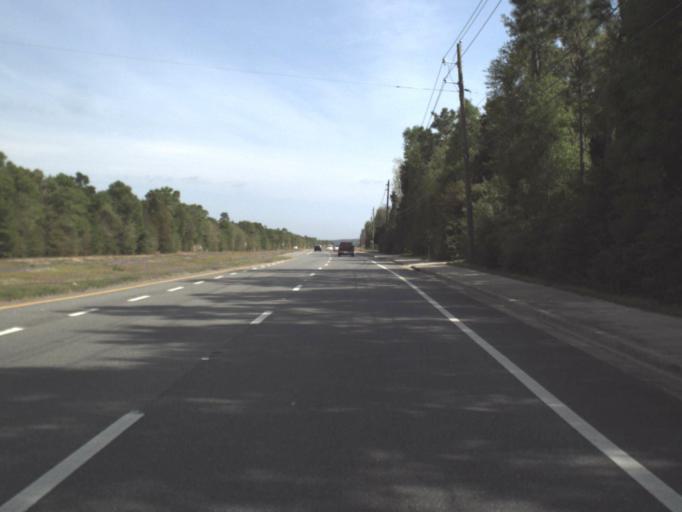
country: US
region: Florida
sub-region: Santa Rosa County
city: East Milton
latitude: 30.6115
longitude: -86.9570
